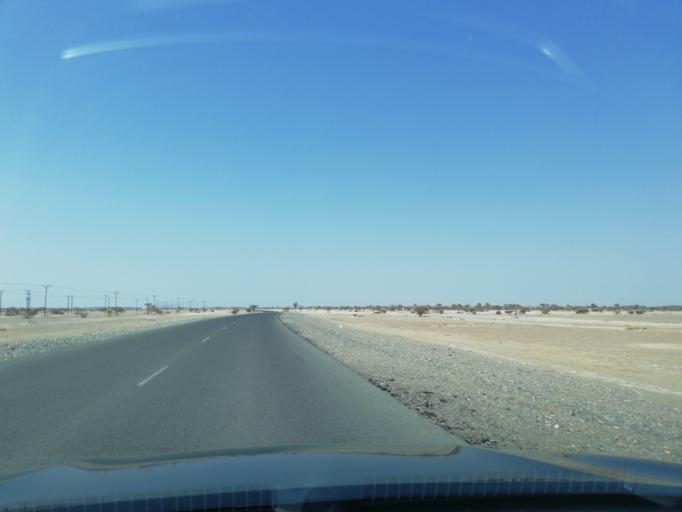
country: OM
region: Muhafazat ad Dakhiliyah
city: Adam
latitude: 22.3419
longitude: 58.0688
